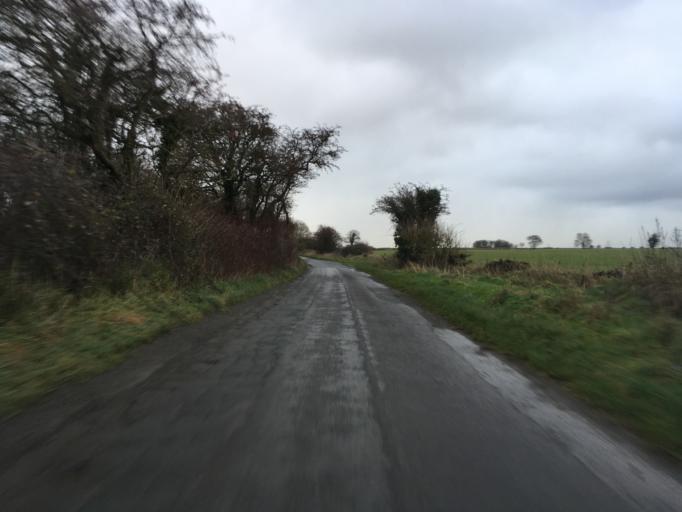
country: GB
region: England
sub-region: South Gloucestershire
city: Marshfield
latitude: 51.4981
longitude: -2.3216
